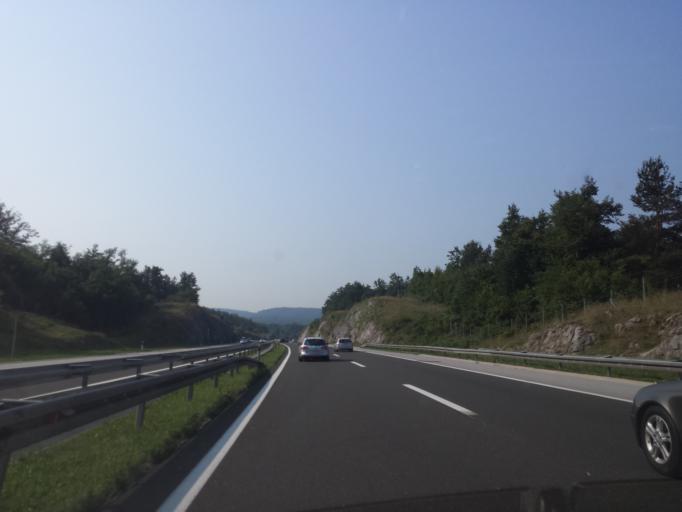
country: HR
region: Karlovacka
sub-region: Grad Ogulin
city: Ogulin
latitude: 45.3049
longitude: 15.2787
